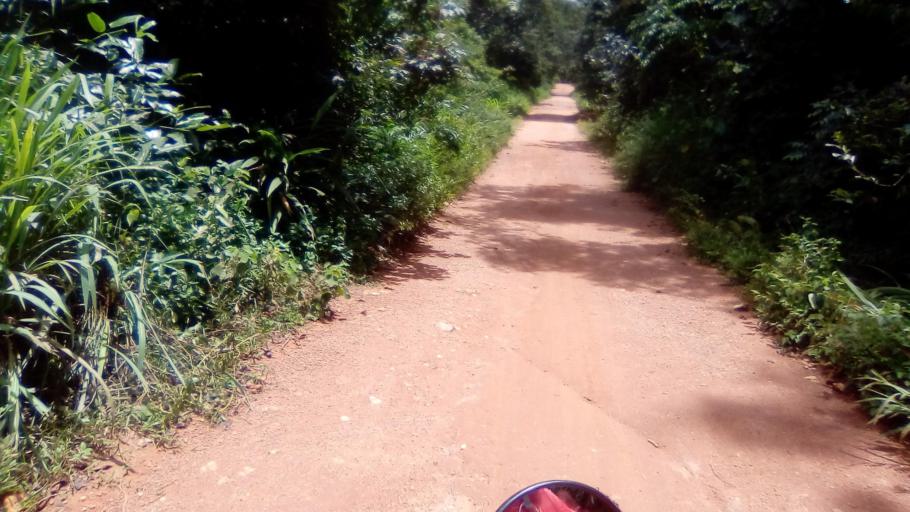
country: SL
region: Eastern Province
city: Simbakoro
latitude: 8.5156
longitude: -10.9081
